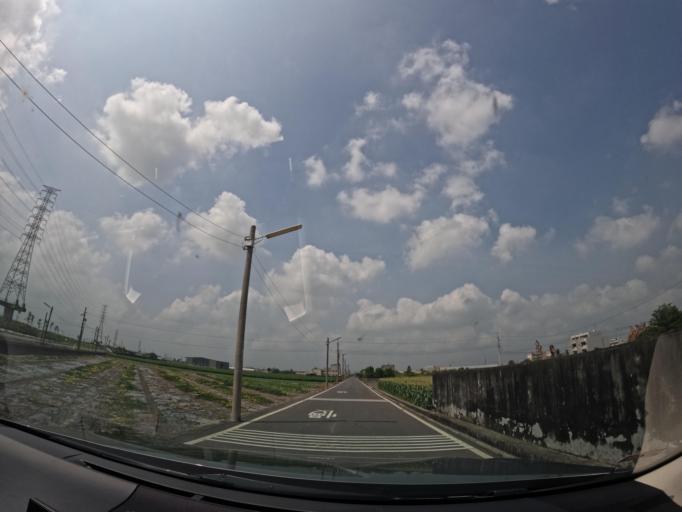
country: TW
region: Taiwan
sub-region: Yunlin
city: Douliu
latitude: 23.6653
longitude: 120.3961
